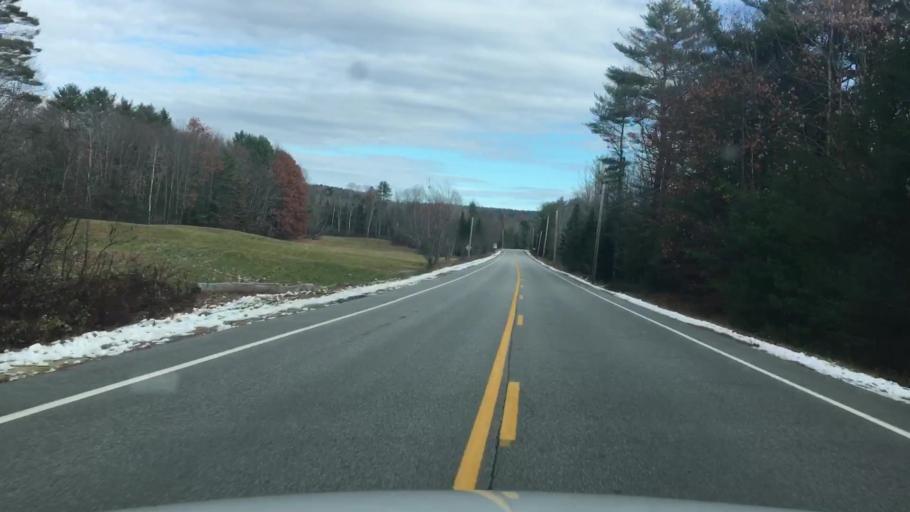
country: US
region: Maine
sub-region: Androscoggin County
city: Leeds
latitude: 44.3461
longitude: -70.1211
